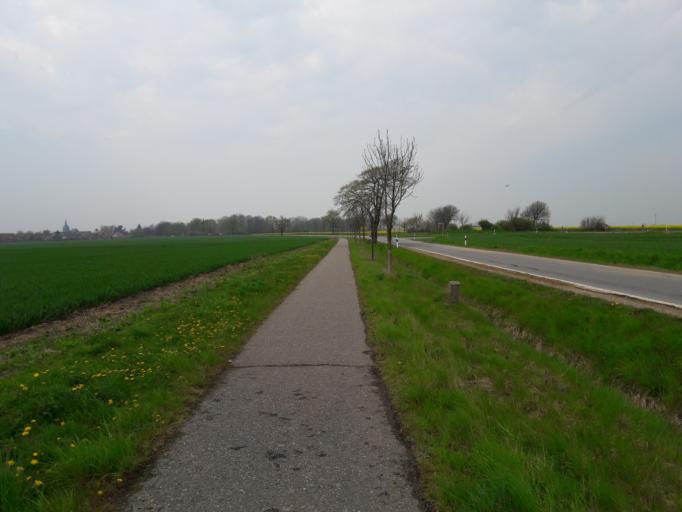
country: DE
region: Schleswig-Holstein
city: Burg auf Fehmarn
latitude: 54.4321
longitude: 11.2159
